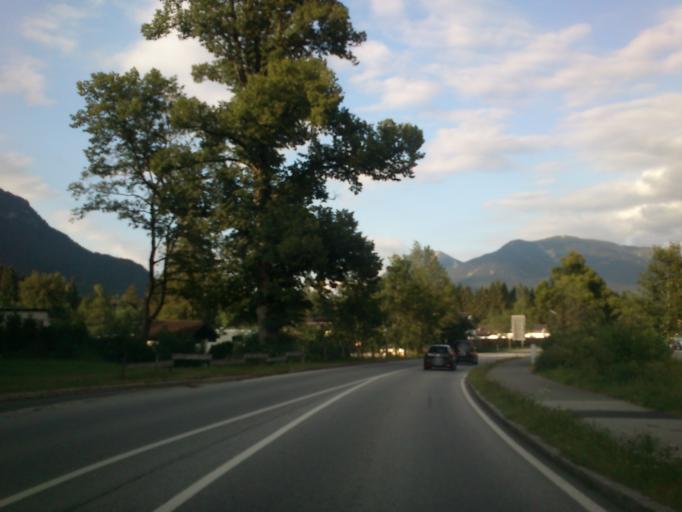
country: DE
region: Bavaria
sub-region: Upper Bavaria
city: Grainau
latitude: 47.4792
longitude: 11.0527
